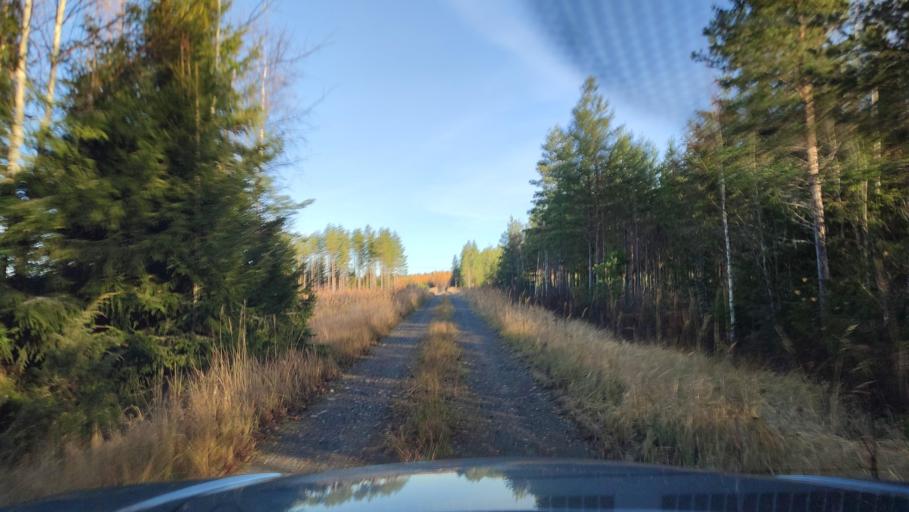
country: FI
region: Southern Ostrobothnia
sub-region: Suupohja
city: Karijoki
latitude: 62.1766
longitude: 21.6072
